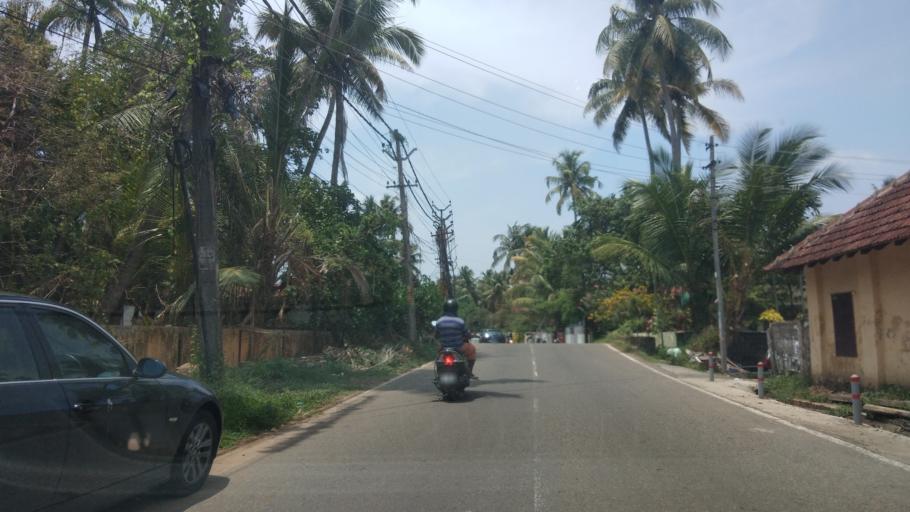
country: IN
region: Kerala
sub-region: Ernakulam
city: Cochin
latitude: 9.8944
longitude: 76.2588
